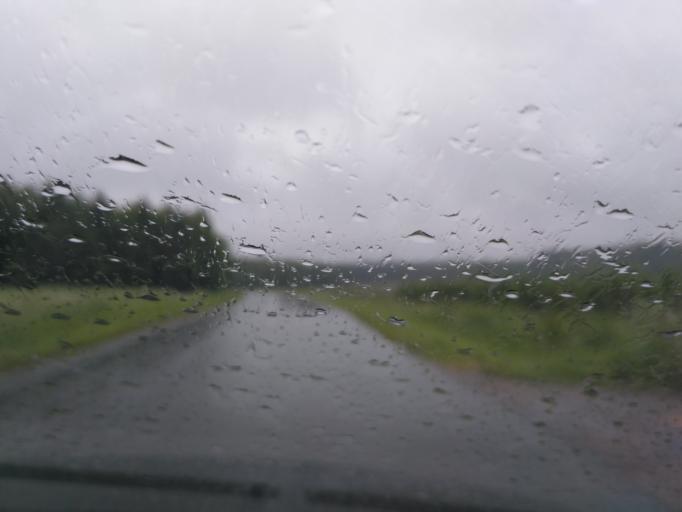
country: PL
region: Subcarpathian Voivodeship
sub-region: Powiat jasielski
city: Debowiec
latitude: 49.6672
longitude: 21.4507
